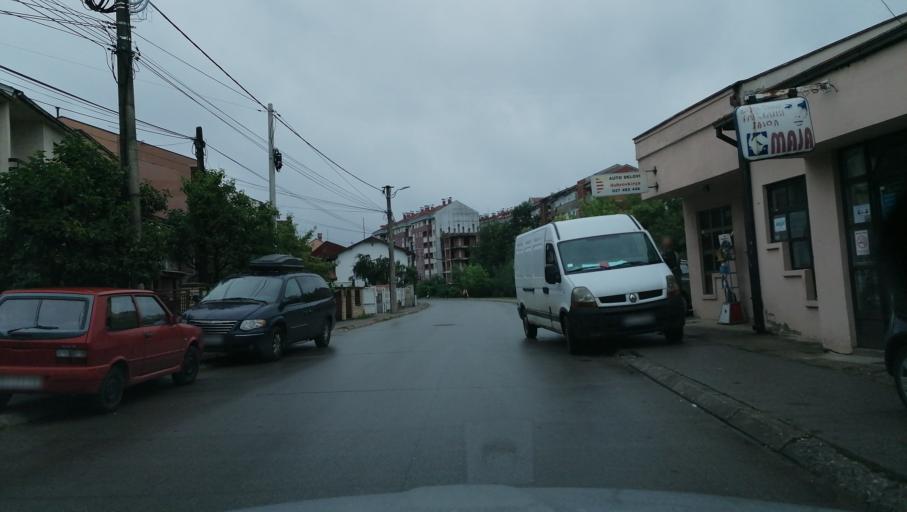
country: RS
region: Central Serbia
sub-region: Rasinski Okrug
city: Krusevac
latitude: 43.5678
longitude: 21.3286
